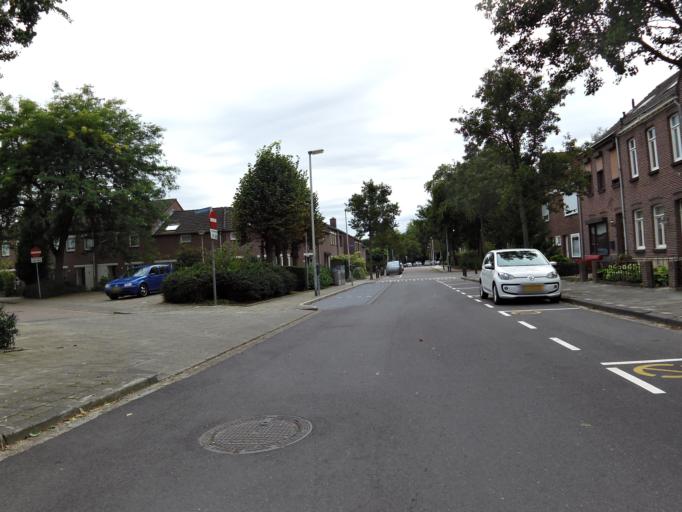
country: NL
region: Limburg
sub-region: Gemeente Heerlen
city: Heerlen
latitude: 50.8904
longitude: 5.9660
